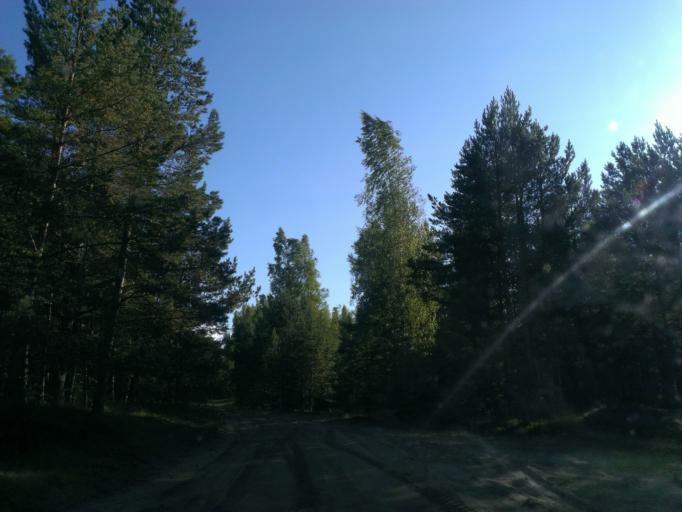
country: LV
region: Adazi
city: Adazi
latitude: 57.0577
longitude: 24.2574
